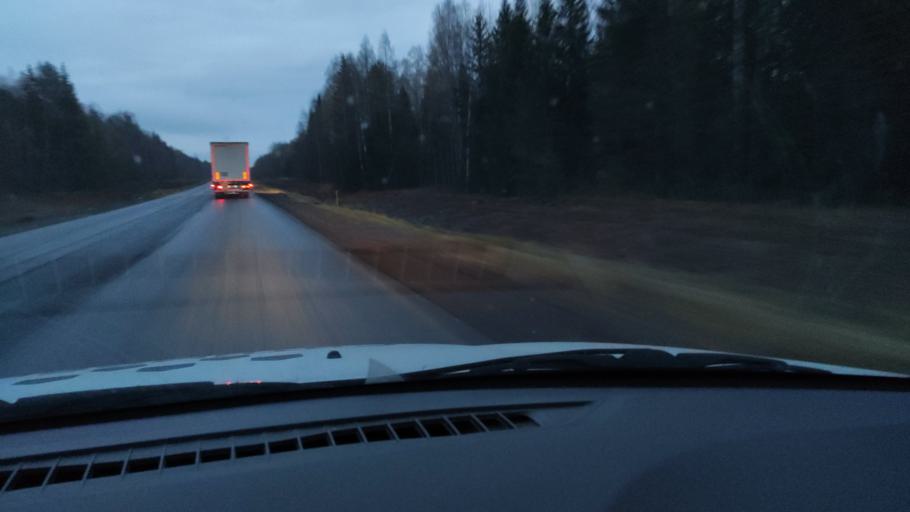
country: RU
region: Kirov
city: Kostino
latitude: 58.8255
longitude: 53.3735
